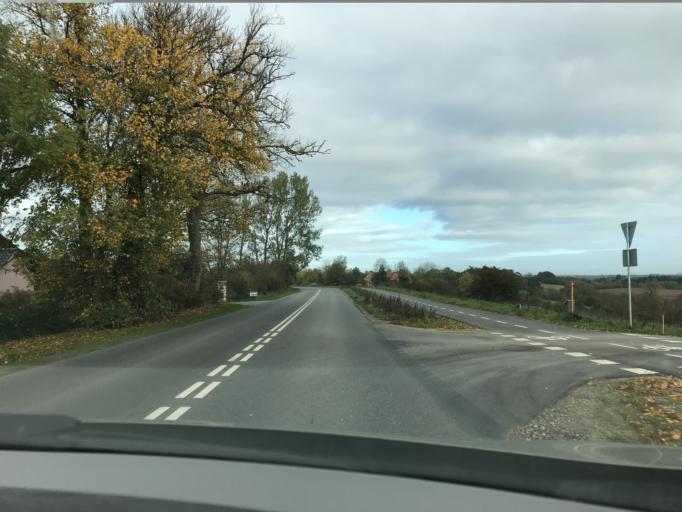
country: DK
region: South Denmark
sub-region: Kolding Kommune
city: Kolding
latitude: 55.5443
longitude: 9.4149
